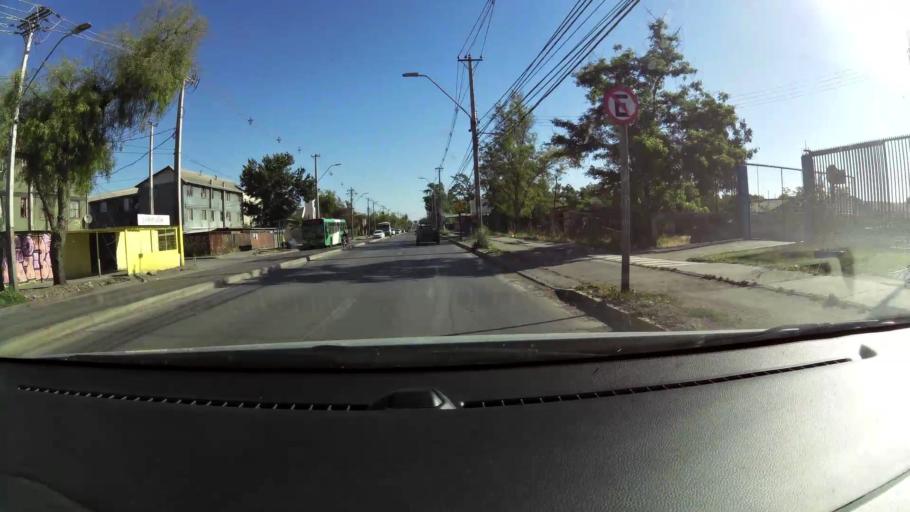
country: CL
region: Santiago Metropolitan
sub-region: Provincia de Maipo
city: San Bernardo
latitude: -33.5954
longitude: -70.6802
